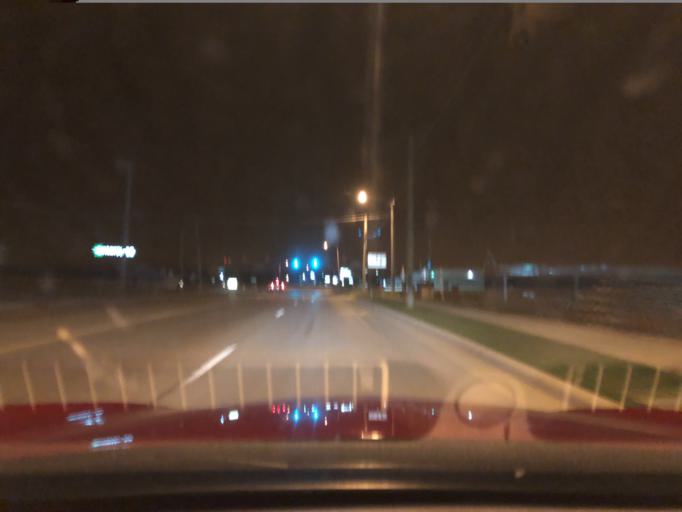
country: US
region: Ohio
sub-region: Logan County
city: Bellefontaine
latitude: 40.3361
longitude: -83.7617
